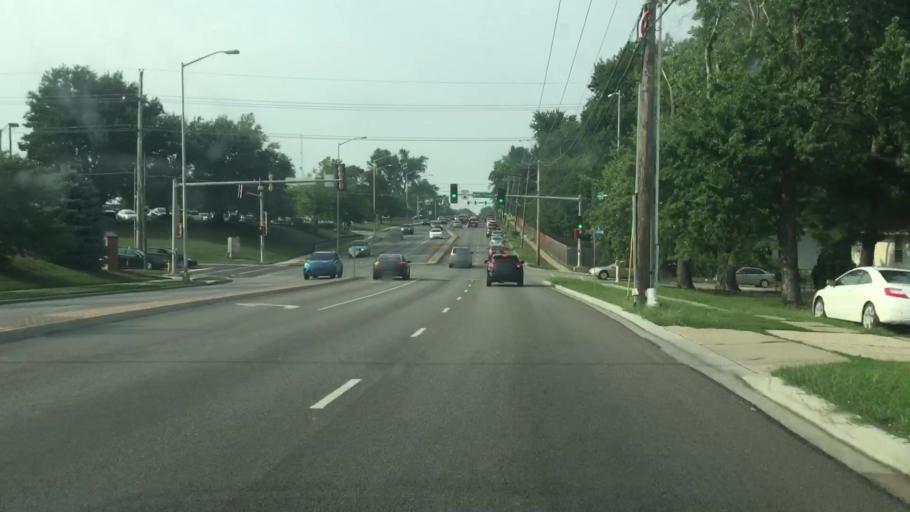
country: US
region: Kansas
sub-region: Johnson County
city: Overland Park
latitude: 38.9707
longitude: -94.6863
